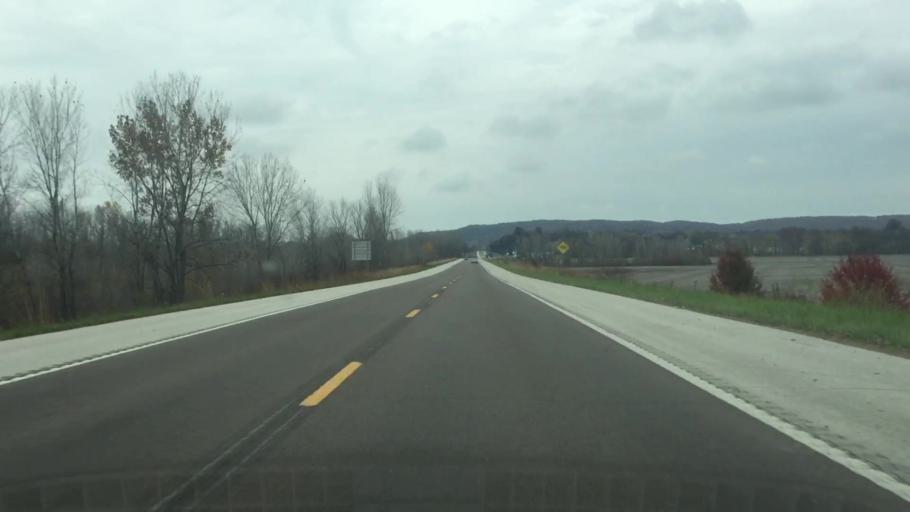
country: US
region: Missouri
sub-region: Gasconade County
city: Hermann
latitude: 38.7212
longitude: -91.4434
